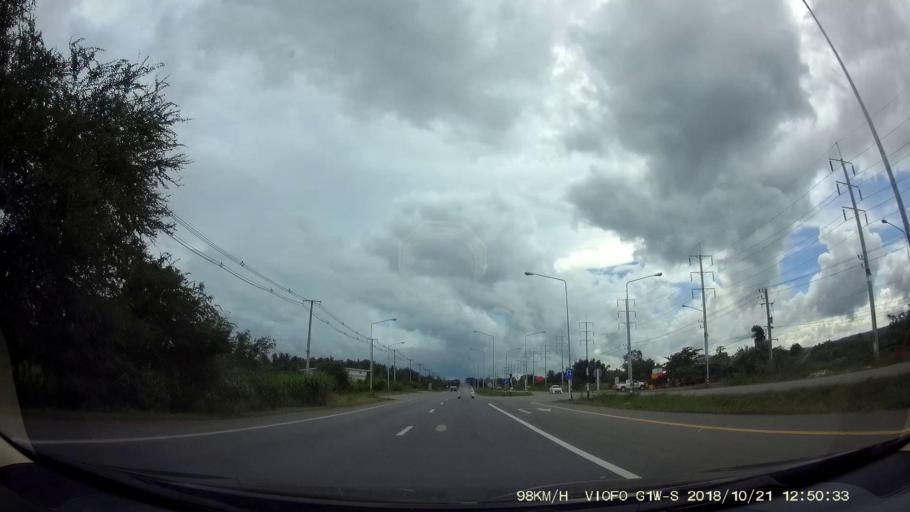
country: TH
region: Nakhon Ratchasima
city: Amphoe Sikhiu
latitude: 14.8806
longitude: 101.6909
